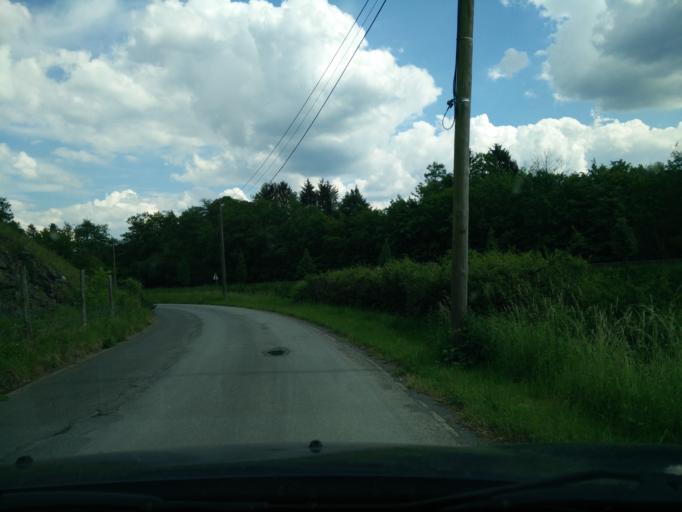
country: BE
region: Wallonia
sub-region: Province de Namur
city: Couvin
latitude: 50.0751
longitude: 4.6012
